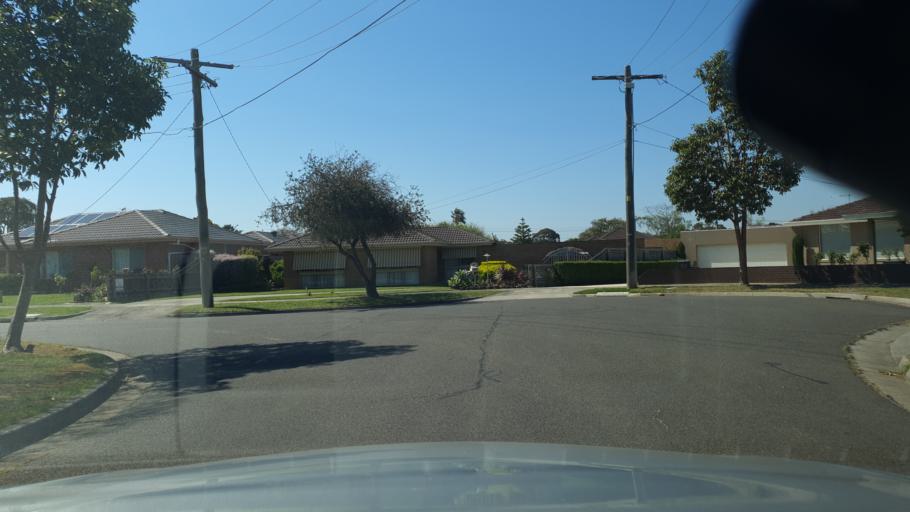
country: AU
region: Victoria
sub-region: Greater Dandenong
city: Springvale
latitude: -37.9334
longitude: 145.1729
